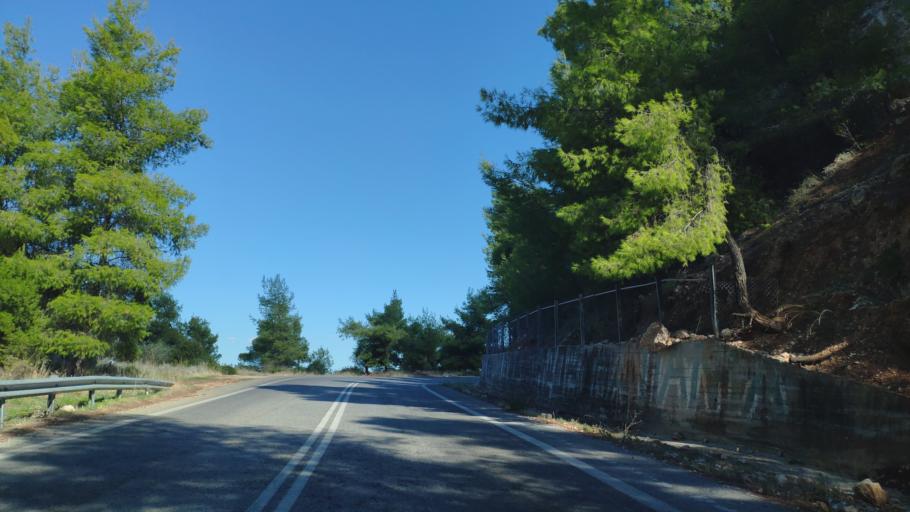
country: GR
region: Peloponnese
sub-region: Nomos Korinthias
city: Sofikon
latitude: 37.8277
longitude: 23.0704
